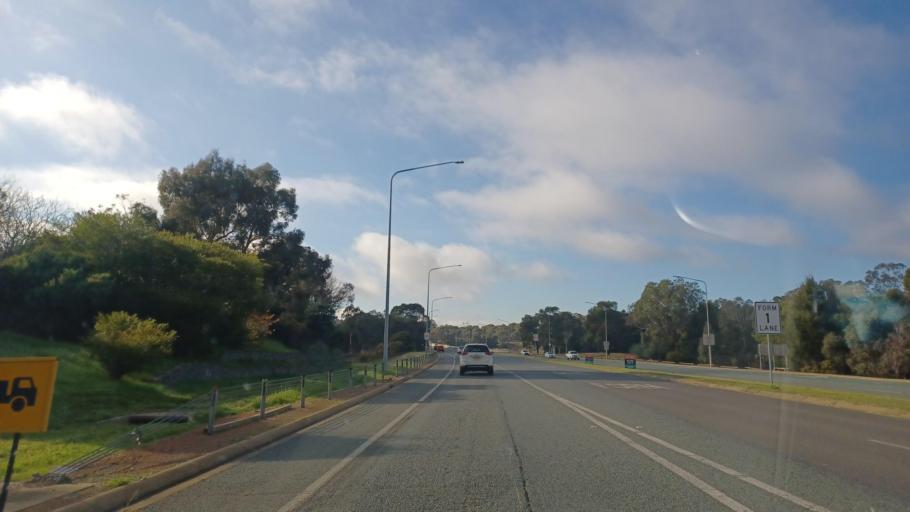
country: AU
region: Australian Capital Territory
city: Belconnen
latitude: -35.2215
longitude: 149.0630
